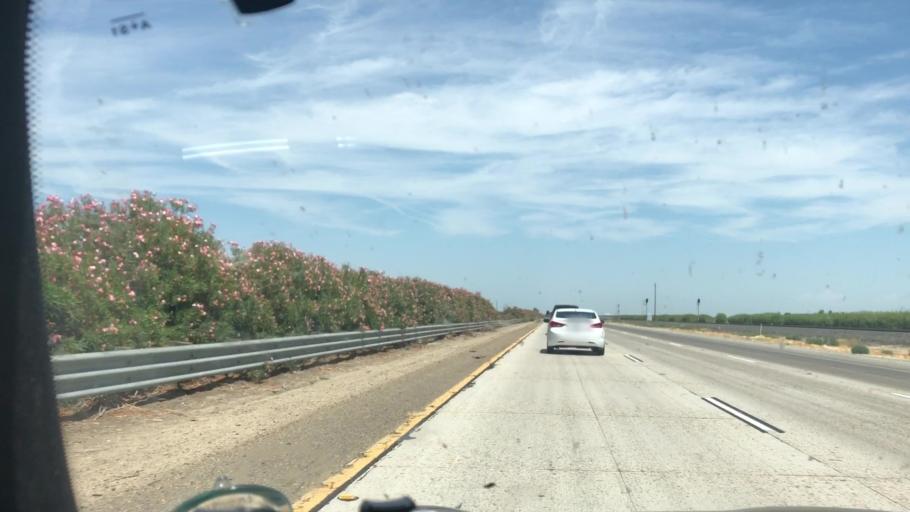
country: US
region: California
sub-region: Kern County
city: McFarland
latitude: 35.6244
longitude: -119.2145
